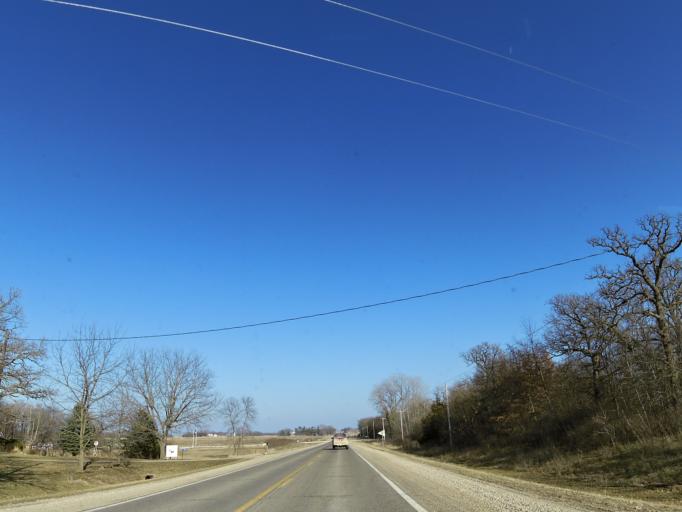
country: US
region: Iowa
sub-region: Worth County
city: Northwood
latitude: 43.4443
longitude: -93.3236
